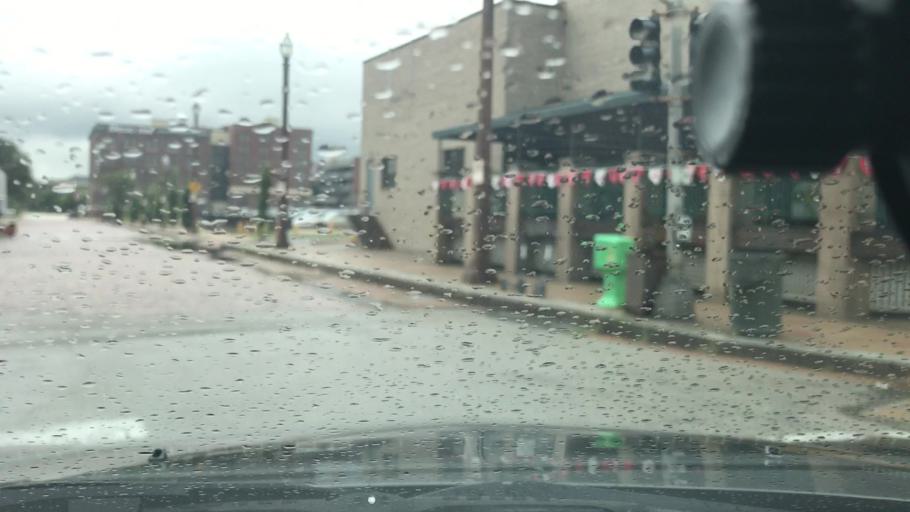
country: US
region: Missouri
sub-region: City of Saint Louis
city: St. Louis
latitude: 38.6298
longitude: -90.2092
